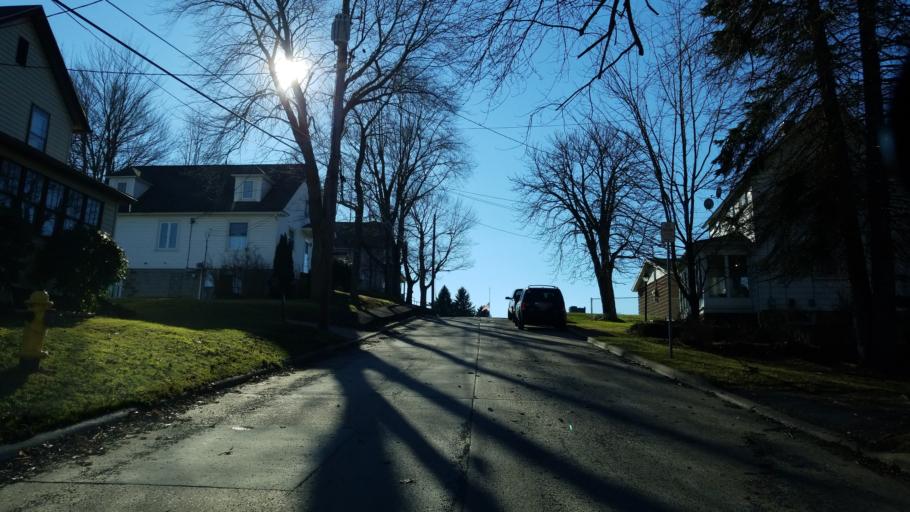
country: US
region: Pennsylvania
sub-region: Clearfield County
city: Sandy
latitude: 41.1235
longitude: -78.7773
